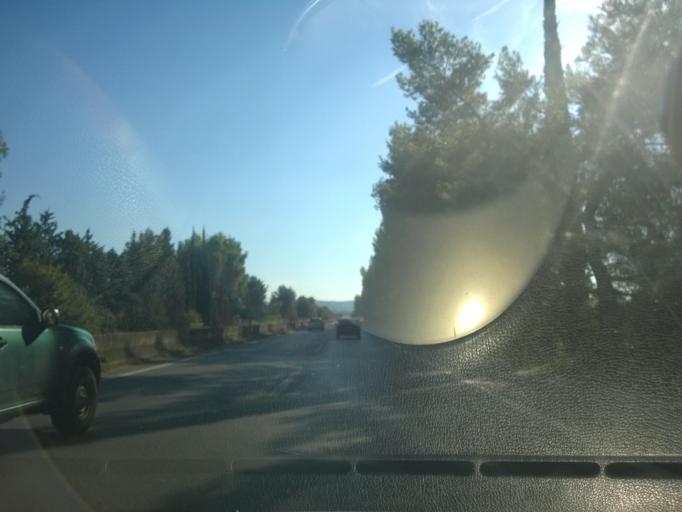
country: GR
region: Central Macedonia
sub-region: Nomos Thessalonikis
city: Thermi
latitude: 40.5235
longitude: 23.0120
